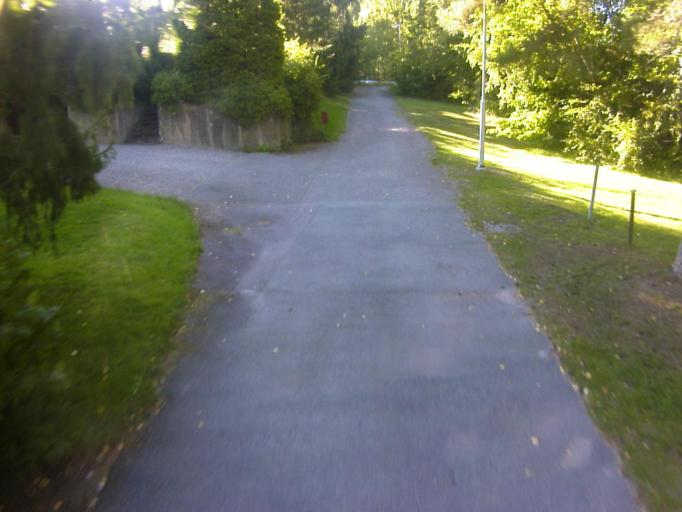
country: SE
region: Soedermanland
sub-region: Eskilstuna Kommun
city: Skogstorp
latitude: 59.3347
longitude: 16.4316
